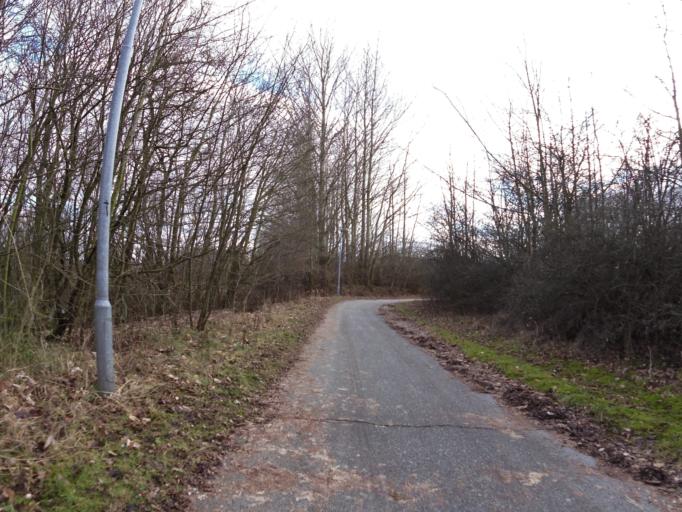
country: DK
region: Central Jutland
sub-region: Arhus Kommune
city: Tranbjerg
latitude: 56.1075
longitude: 10.1189
